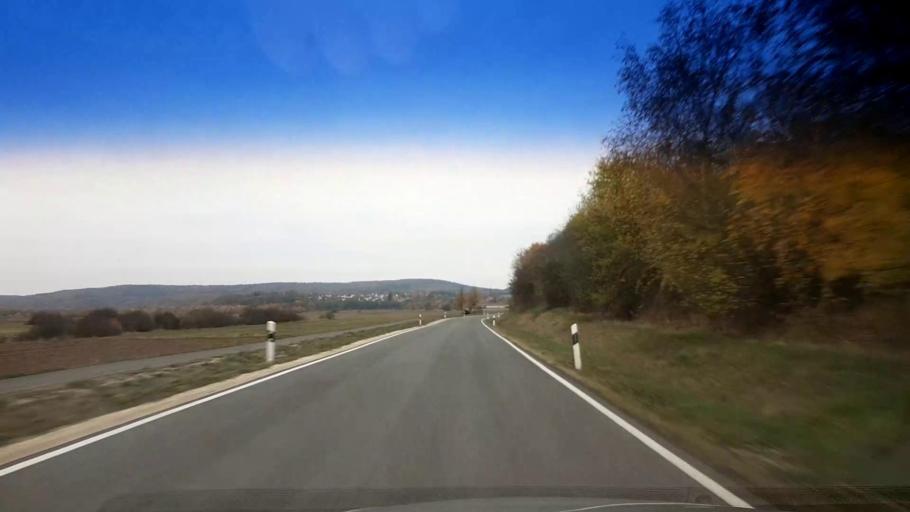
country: DE
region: Bavaria
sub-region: Upper Franconia
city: Baunach
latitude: 49.9968
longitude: 10.8688
